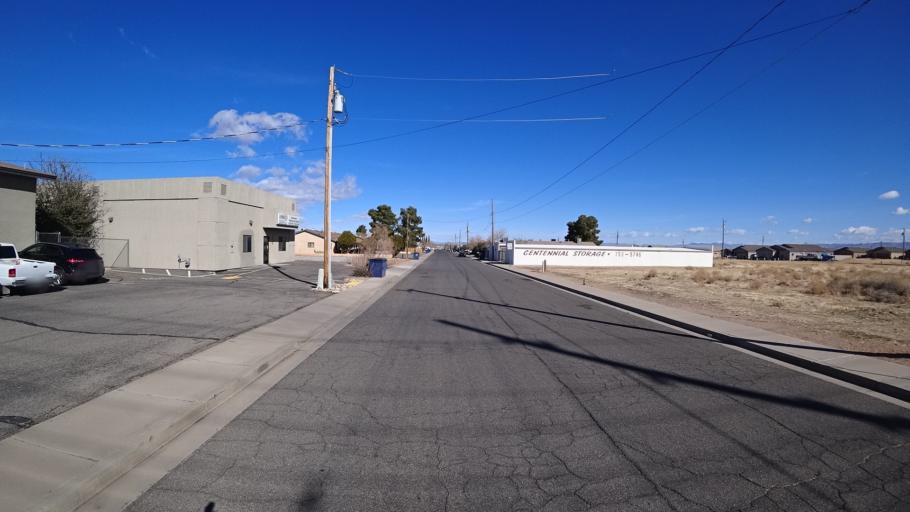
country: US
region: Arizona
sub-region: Mohave County
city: New Kingman-Butler
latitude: 35.2251
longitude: -114.0241
